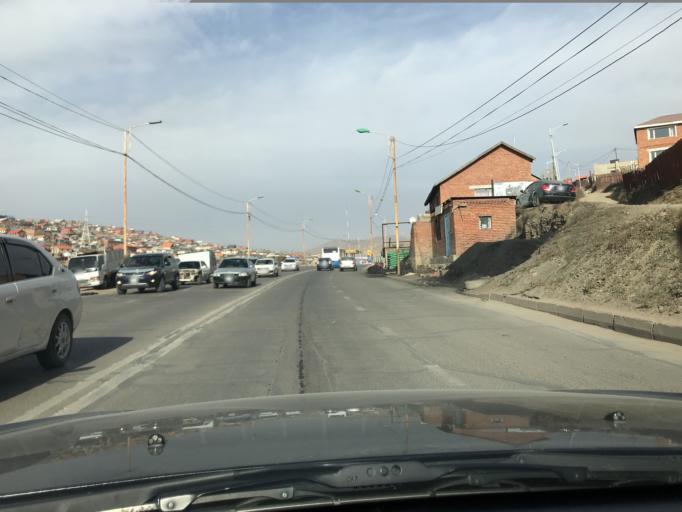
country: MN
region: Ulaanbaatar
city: Ulaanbaatar
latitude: 47.9352
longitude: 106.8849
